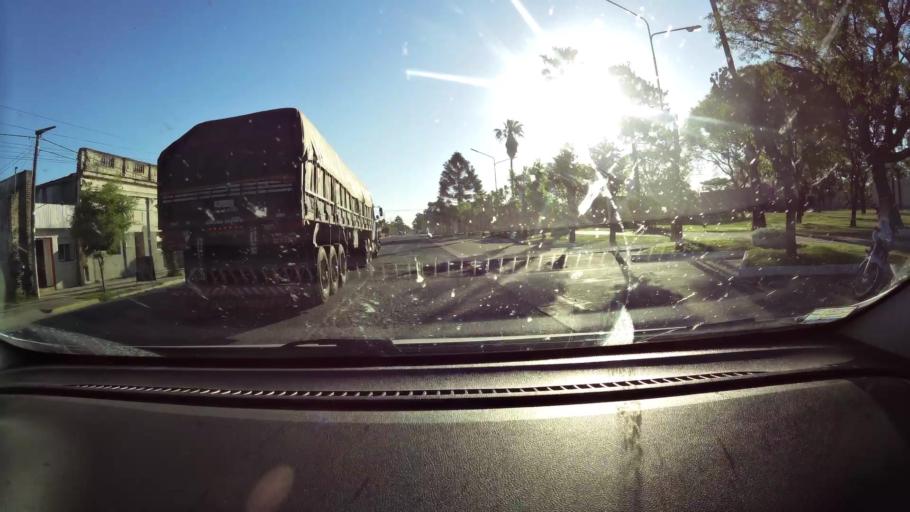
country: AR
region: Cordoba
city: Saturnino M. Laspiur
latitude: -31.7040
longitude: -62.4830
